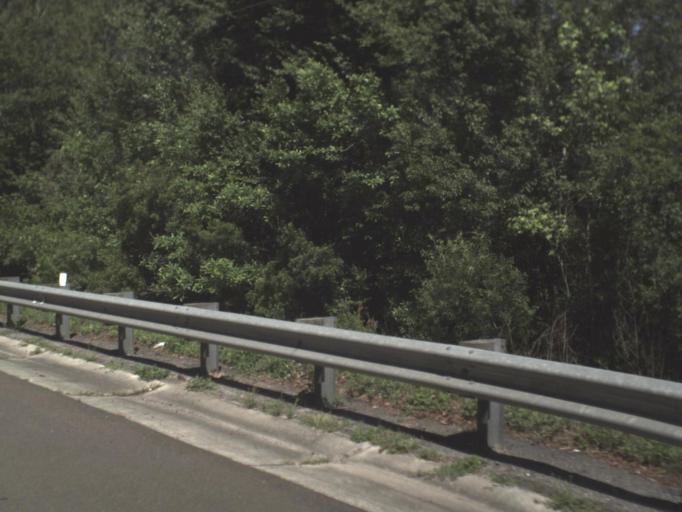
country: US
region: Florida
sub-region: Duval County
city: Baldwin
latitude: 30.3003
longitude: -82.0308
